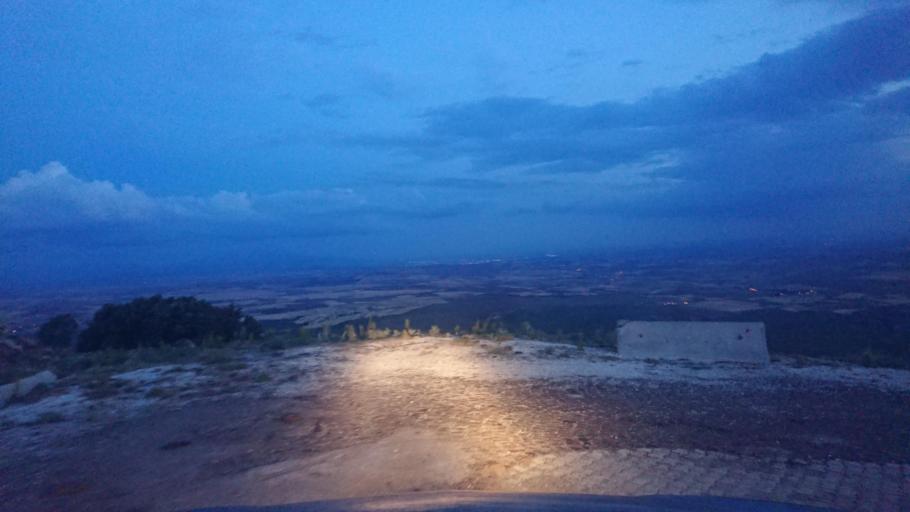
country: TR
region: Aksaray
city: Ortakoy
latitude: 38.6390
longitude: 34.0274
